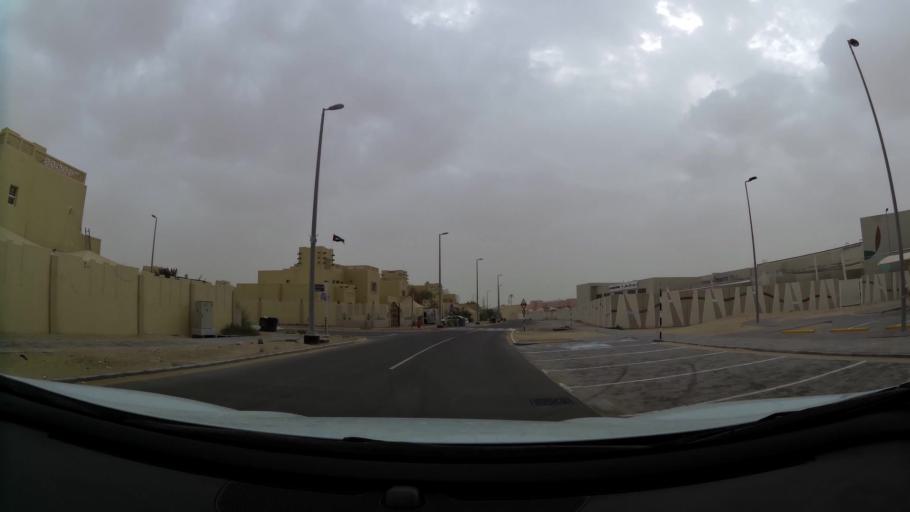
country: AE
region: Abu Dhabi
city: Abu Dhabi
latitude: 24.4476
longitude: 54.7110
